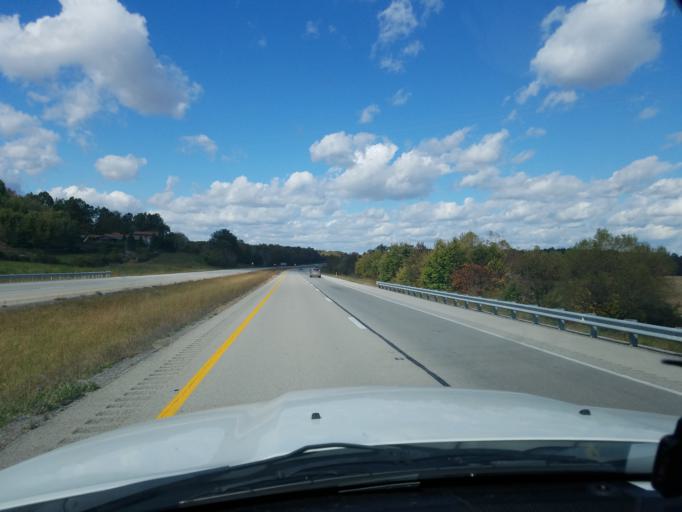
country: US
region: Kentucky
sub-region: Daviess County
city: Masonville
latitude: 37.6032
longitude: -86.9752
